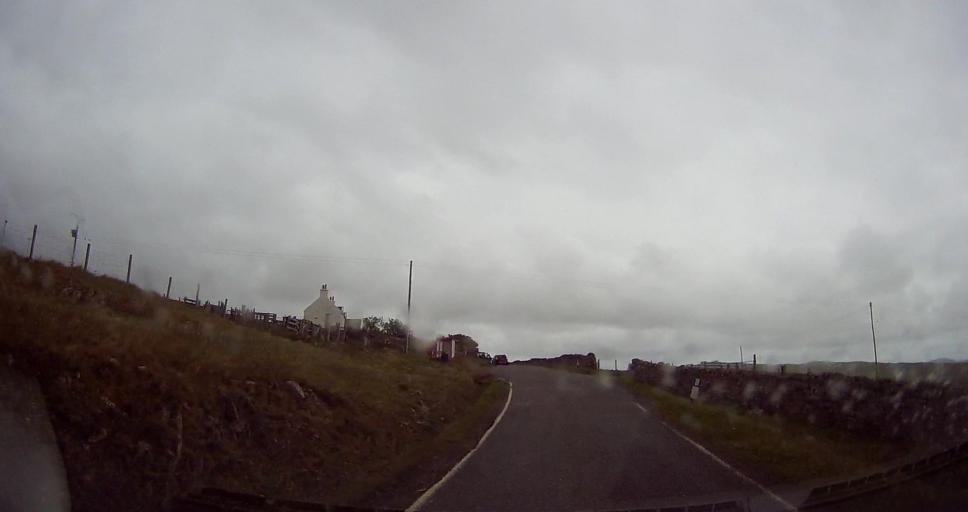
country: GB
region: Scotland
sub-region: Shetland Islands
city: Sandwick
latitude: 60.2443
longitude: -1.5254
